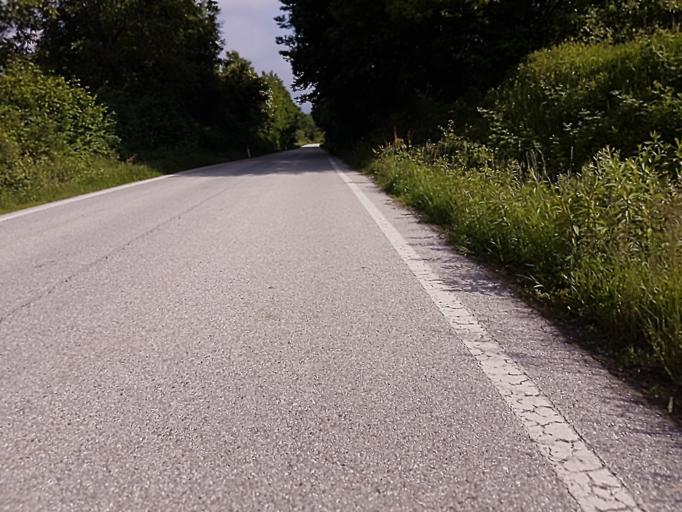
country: IT
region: Piedmont
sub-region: Provincia di Torino
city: Vialfre
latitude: 45.3863
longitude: 7.8172
